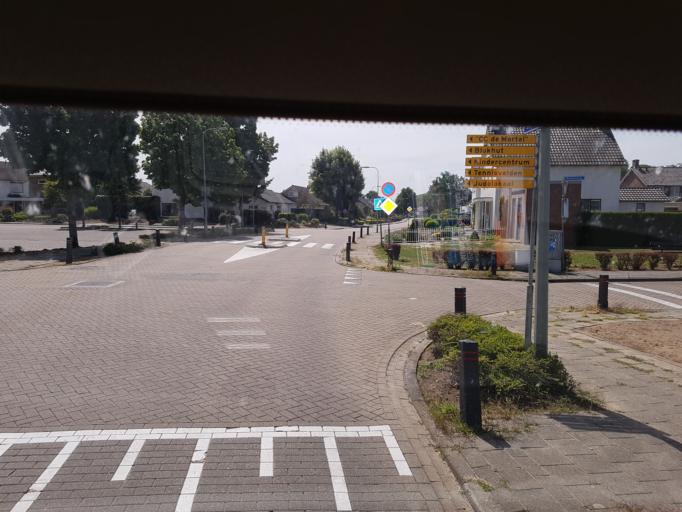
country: NL
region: Limburg
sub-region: Gemeente Leudal
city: Kelpen-Oler
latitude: 51.1730
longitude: 5.8234
